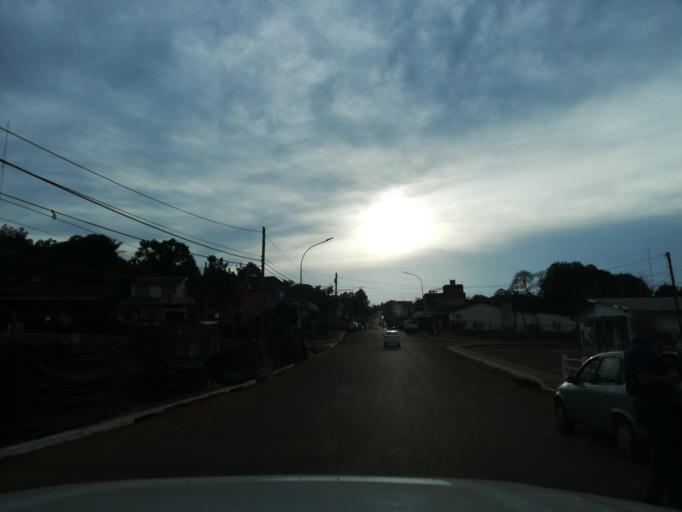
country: AR
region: Misiones
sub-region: Departamento de San Pedro
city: San Pedro
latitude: -26.6243
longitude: -54.1127
